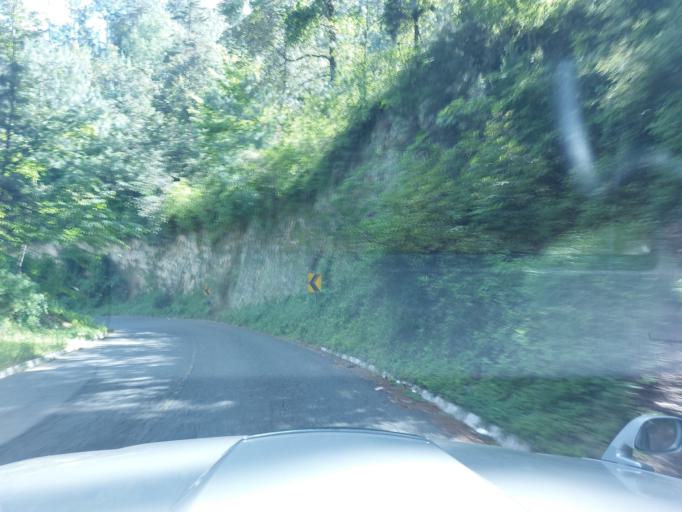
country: GT
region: Chimaltenango
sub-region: Municipio de Santa Cruz Balanya
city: Santa Cruz Balanya
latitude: 14.6916
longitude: -90.8973
